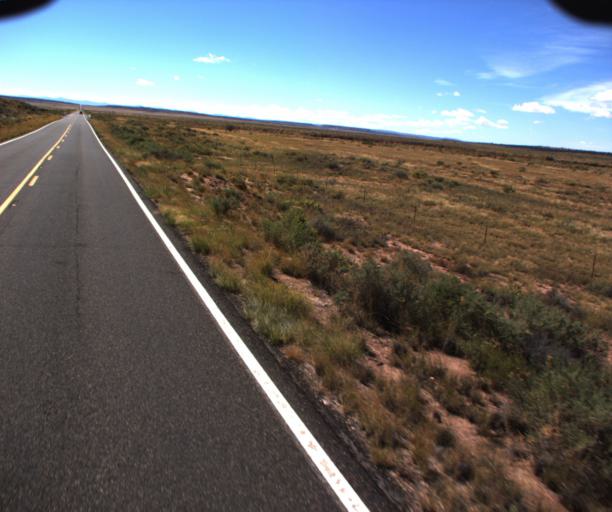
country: US
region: Arizona
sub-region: Apache County
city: Saint Johns
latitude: 34.7203
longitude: -109.2600
